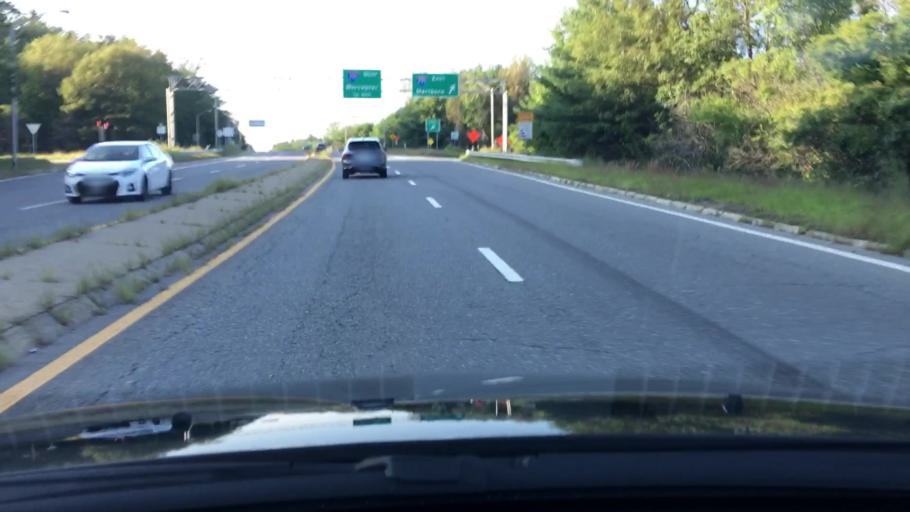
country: US
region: Massachusetts
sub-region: Worcester County
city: Shrewsbury
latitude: 42.3185
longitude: -71.7182
